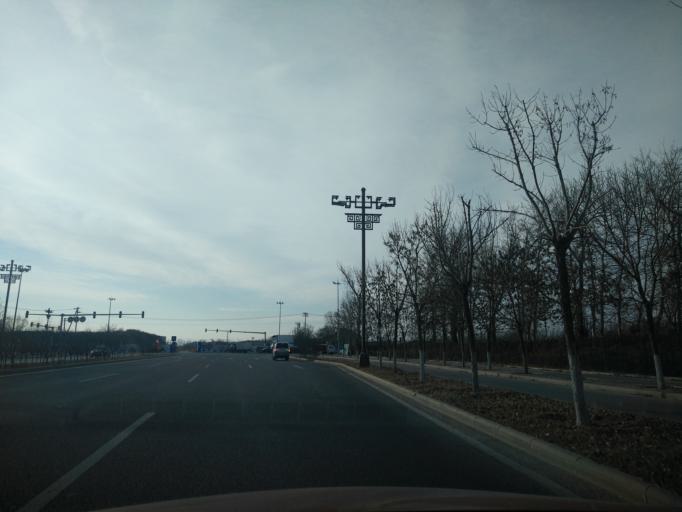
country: CN
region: Beijing
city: Jiugong
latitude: 39.7867
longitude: 116.4475
